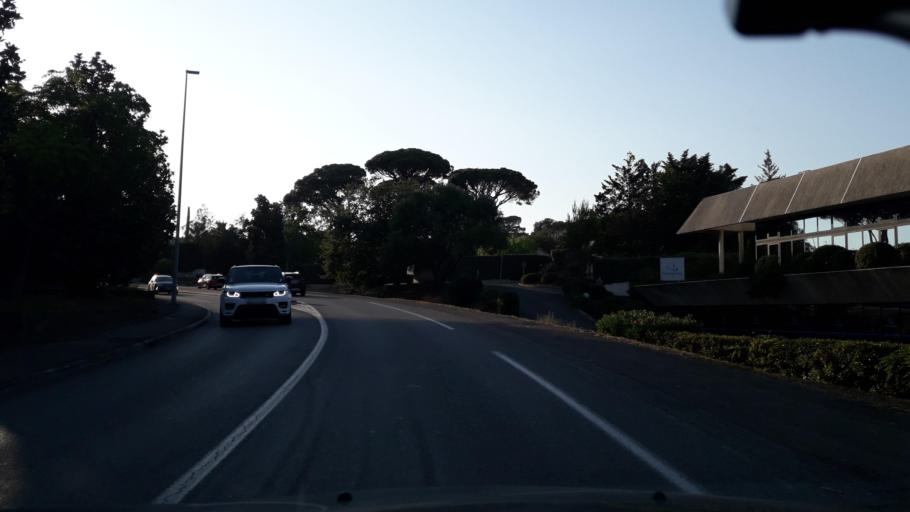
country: FR
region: Provence-Alpes-Cote d'Azur
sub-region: Departement du Var
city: Saint-Raphael
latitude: 43.4403
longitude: 6.7830
